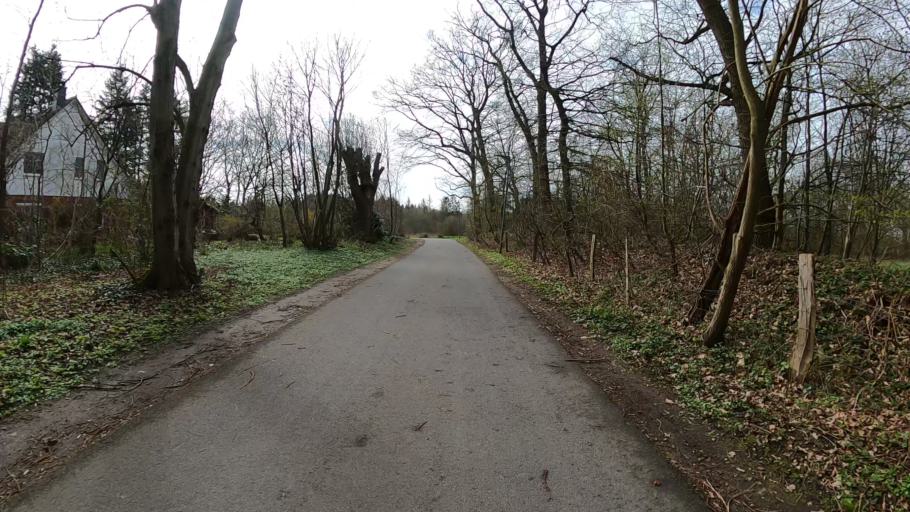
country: DE
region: Schleswig-Holstein
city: Stapelfeld
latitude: 53.6382
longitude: 10.2078
